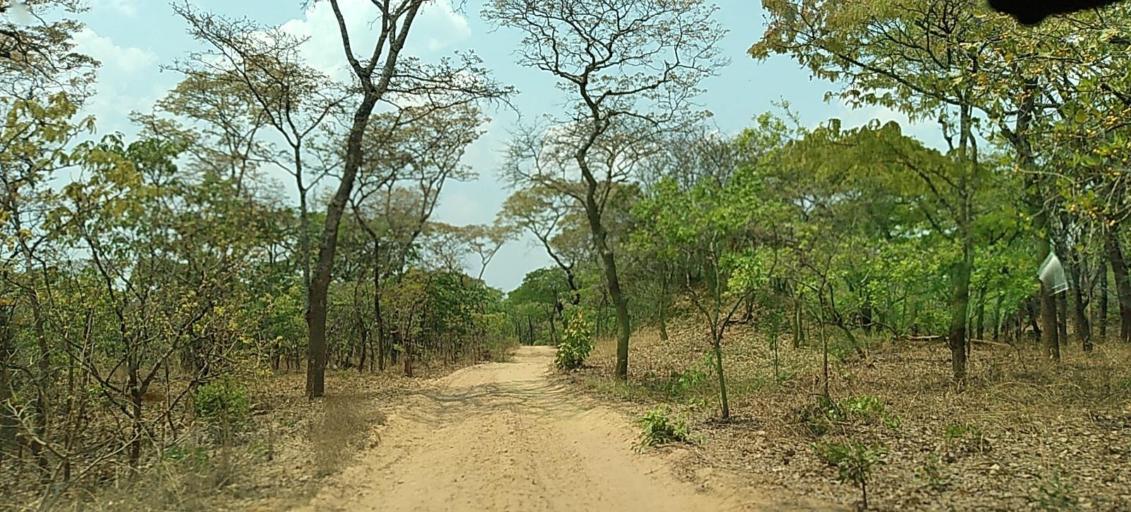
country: ZM
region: North-Western
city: Kabompo
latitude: -13.6393
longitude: 24.3835
